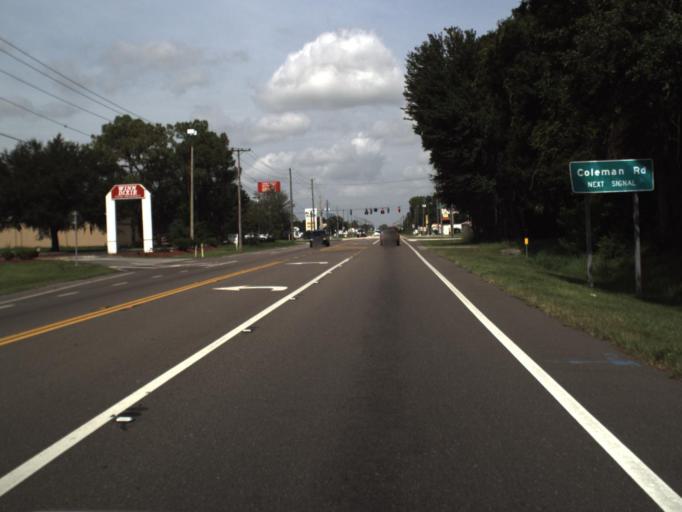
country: US
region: Florida
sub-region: Polk County
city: Jan-Phyl Village
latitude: 28.0160
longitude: -81.7577
